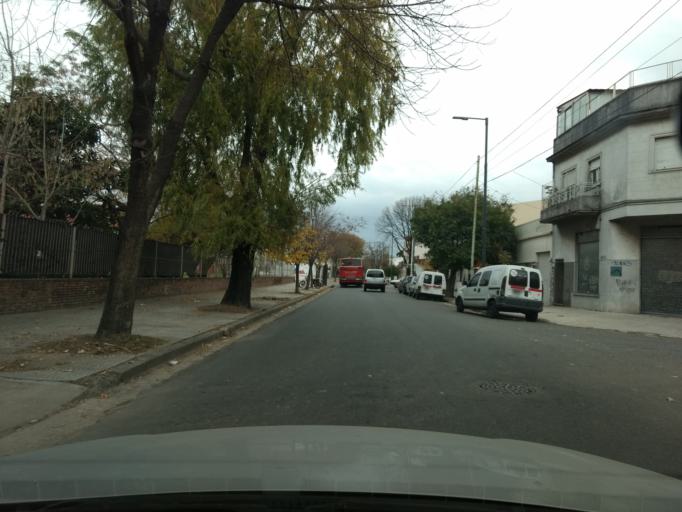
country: AR
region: Buenos Aires F.D.
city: Villa Santa Rita
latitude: -34.6214
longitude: -58.5183
